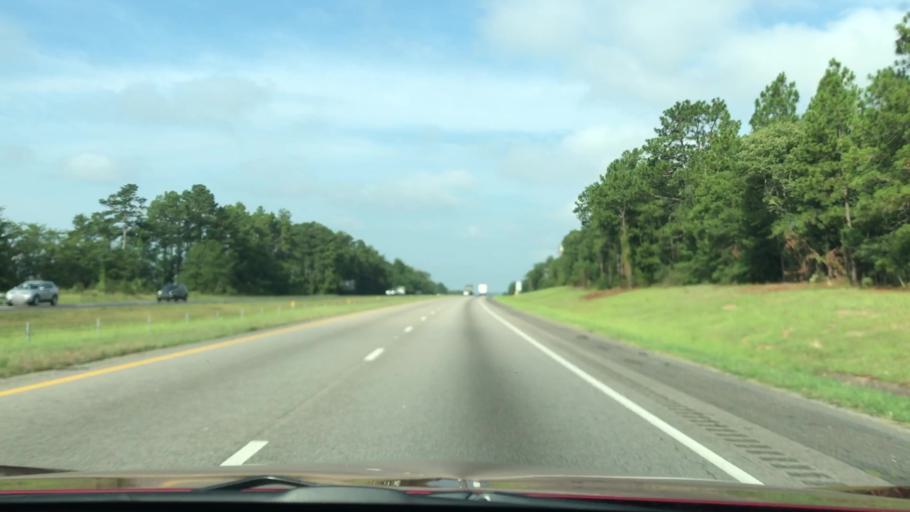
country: US
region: South Carolina
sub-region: Aiken County
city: Aiken
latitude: 33.6608
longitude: -81.6864
